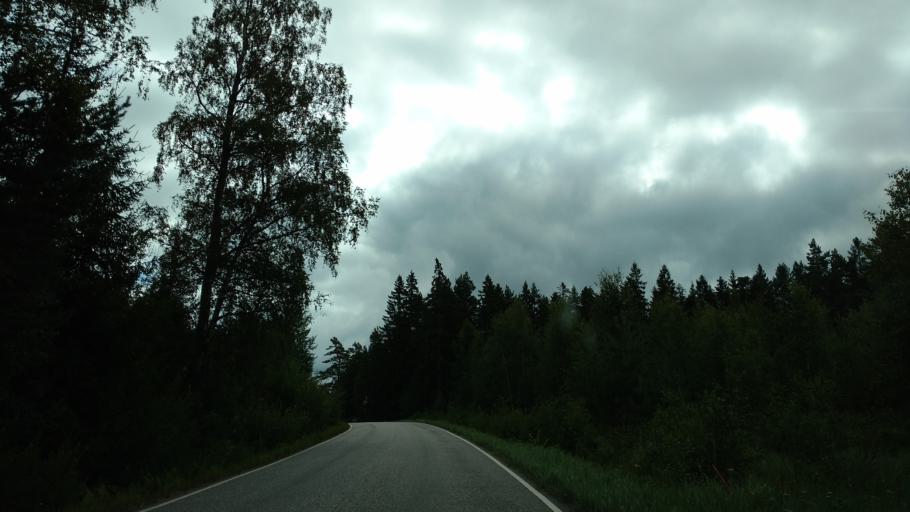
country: FI
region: Varsinais-Suomi
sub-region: Aboland-Turunmaa
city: Dragsfjaerd
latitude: 60.0302
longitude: 22.4482
